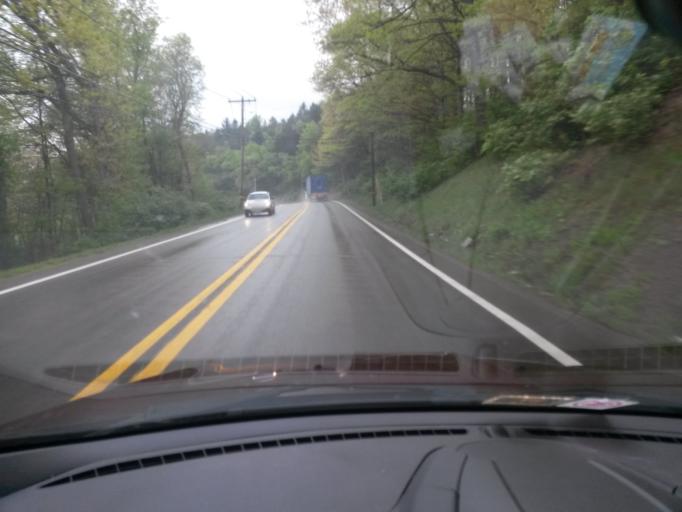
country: US
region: West Virginia
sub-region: Randolph County
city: Elkins
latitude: 38.8281
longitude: -79.8736
